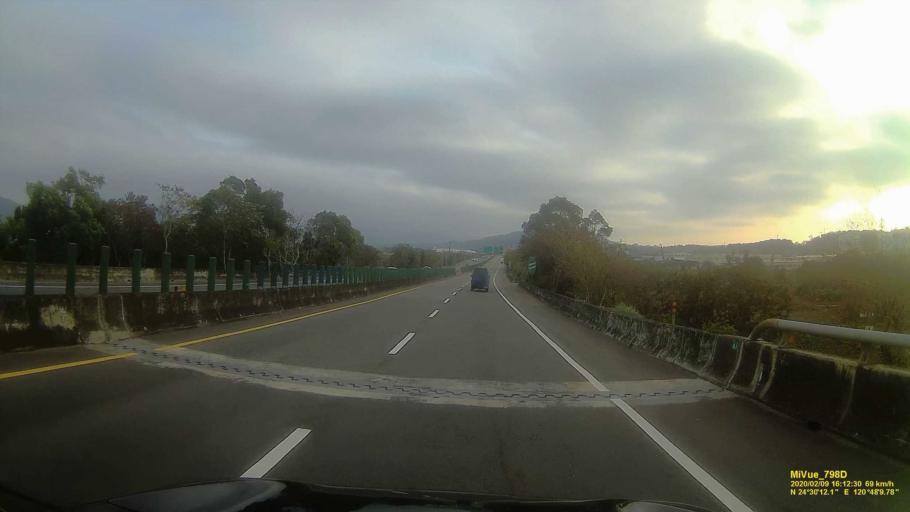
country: TW
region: Taiwan
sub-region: Miaoli
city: Miaoli
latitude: 24.5029
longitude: 120.8027
